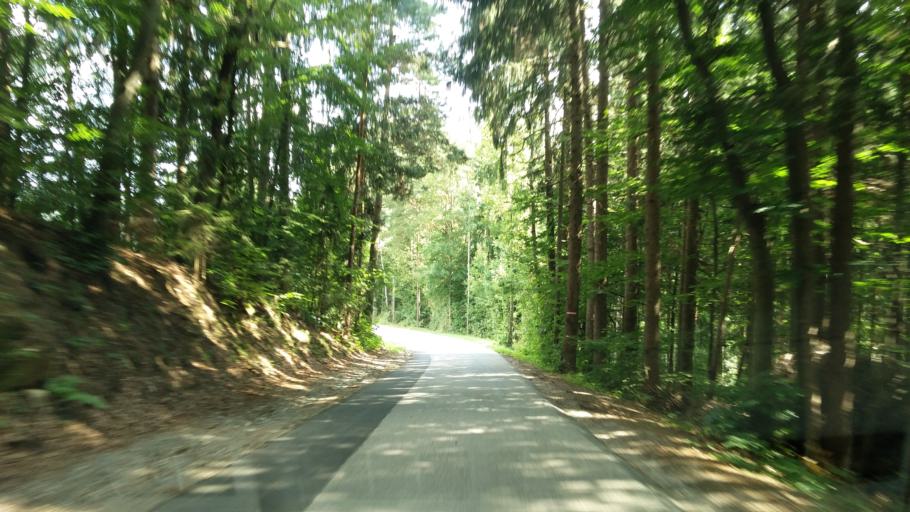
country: AT
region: Styria
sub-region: Politischer Bezirk Weiz
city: Naas
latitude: 47.2535
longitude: 15.6012
